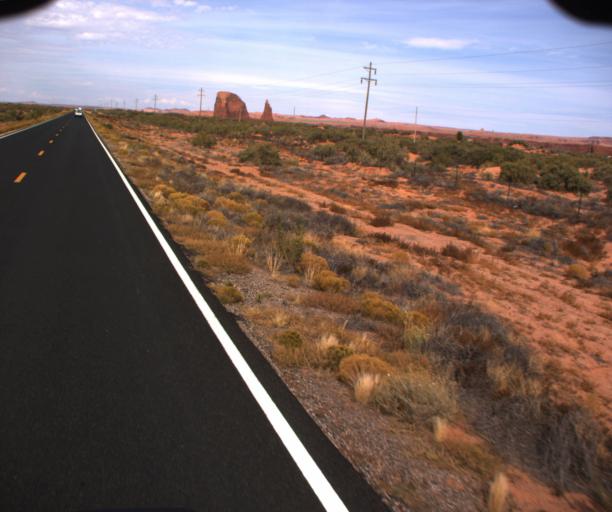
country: US
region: Arizona
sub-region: Apache County
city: Many Farms
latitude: 36.6318
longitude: -109.5854
